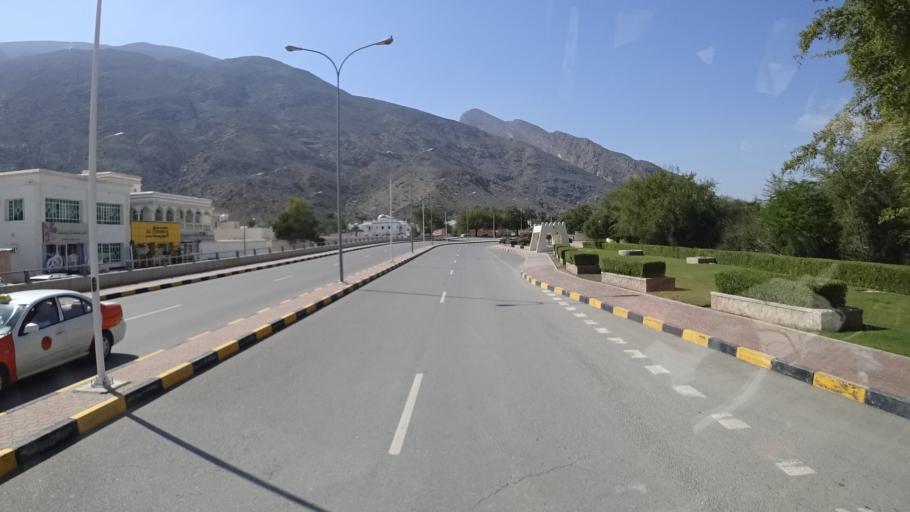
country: OM
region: Al Batinah
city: Rustaq
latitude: 23.3884
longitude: 57.4246
